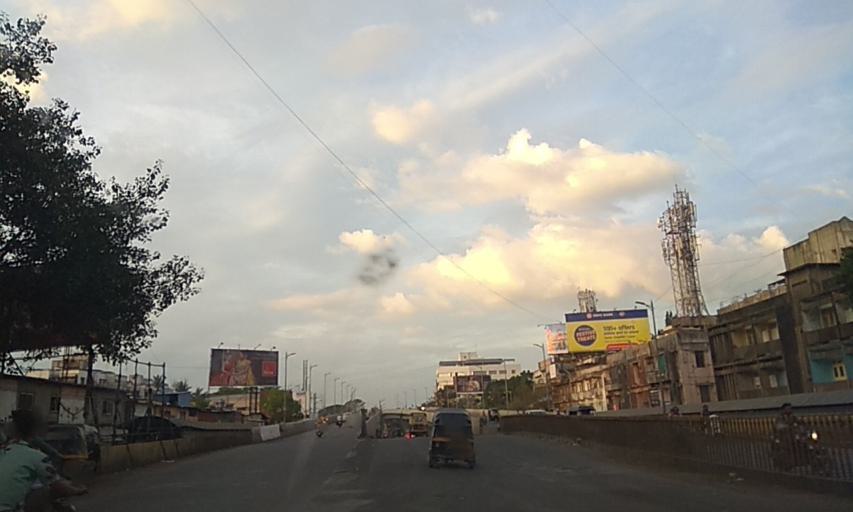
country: IN
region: Maharashtra
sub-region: Pune Division
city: Pune
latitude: 18.4941
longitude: 73.8578
